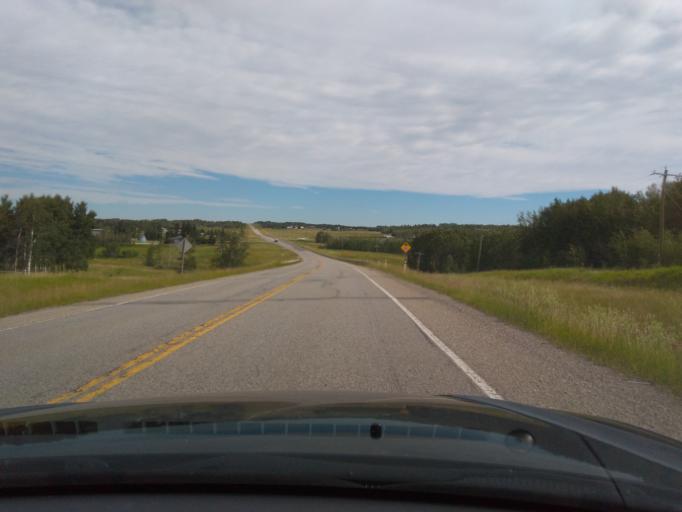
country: CA
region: Alberta
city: Cochrane
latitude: 51.3685
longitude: -114.4706
